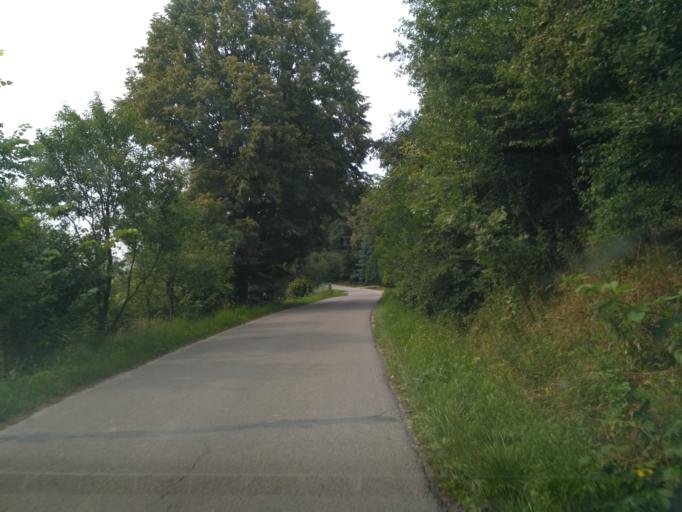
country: PL
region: Subcarpathian Voivodeship
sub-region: Powiat strzyzowski
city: Strzyzow
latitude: 49.8541
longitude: 21.8034
